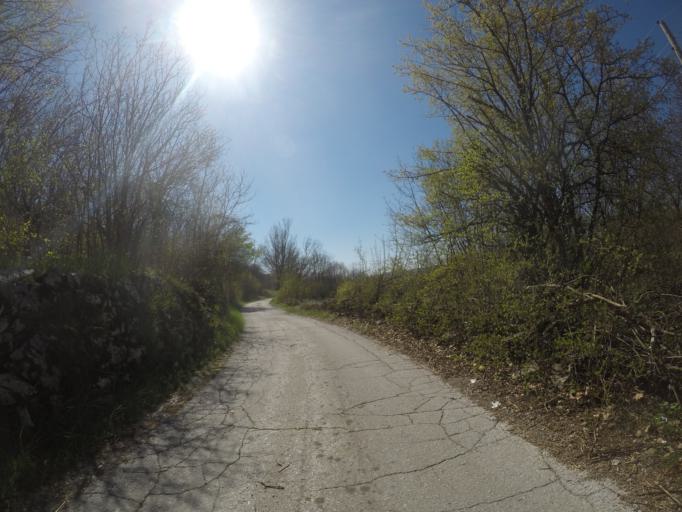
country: ME
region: Danilovgrad
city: Danilovgrad
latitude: 42.5411
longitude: 19.0100
